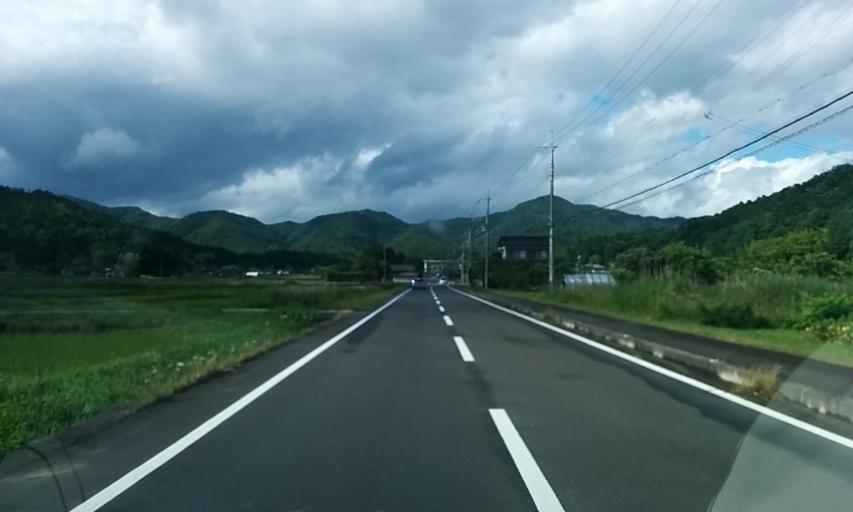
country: JP
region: Kyoto
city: Ayabe
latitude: 35.3761
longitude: 135.2365
